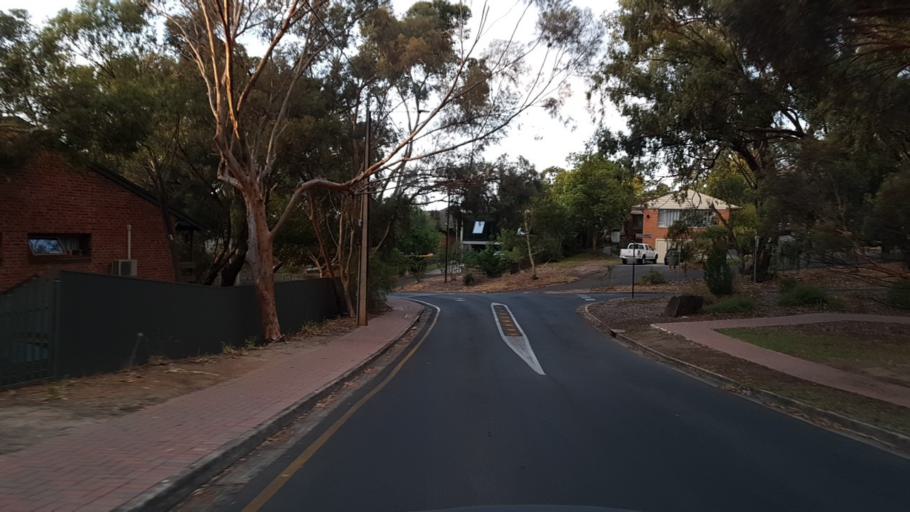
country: AU
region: South Australia
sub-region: Burnside
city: Hazelwood Park
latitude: -34.9393
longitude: 138.6683
